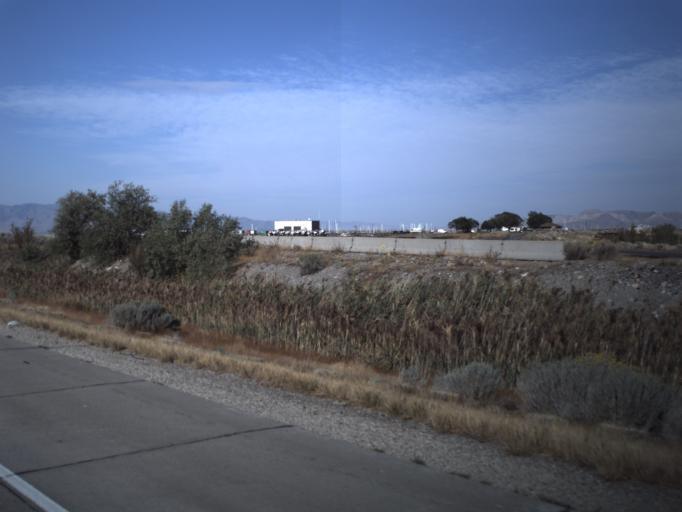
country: US
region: Utah
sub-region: Salt Lake County
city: Magna
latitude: 40.7325
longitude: -112.2039
